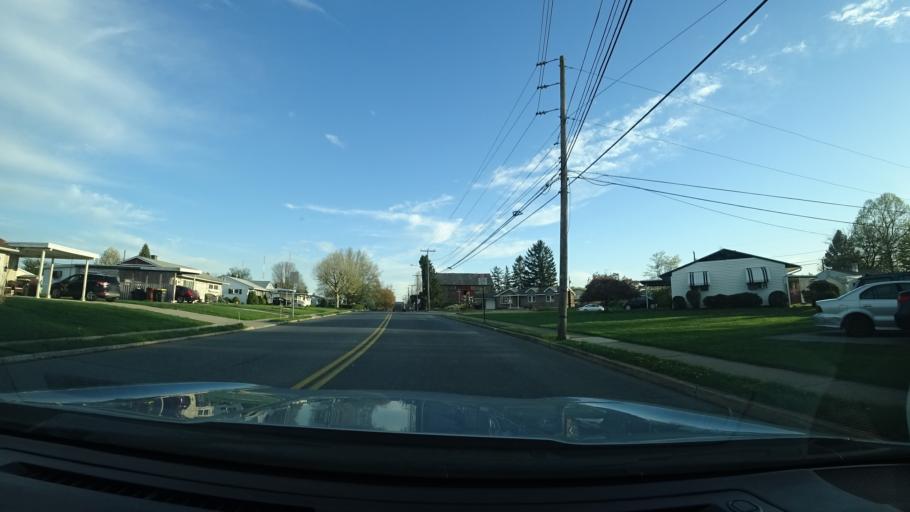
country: US
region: Pennsylvania
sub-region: Lehigh County
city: Fullerton
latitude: 40.6408
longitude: -75.4854
